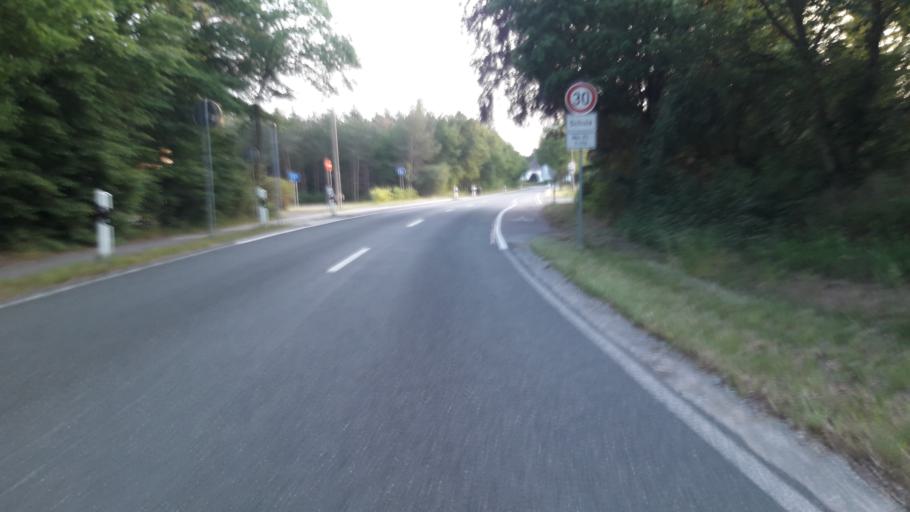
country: DE
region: North Rhine-Westphalia
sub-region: Regierungsbezirk Detmold
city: Hovelhof
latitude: 51.8670
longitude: 8.6462
